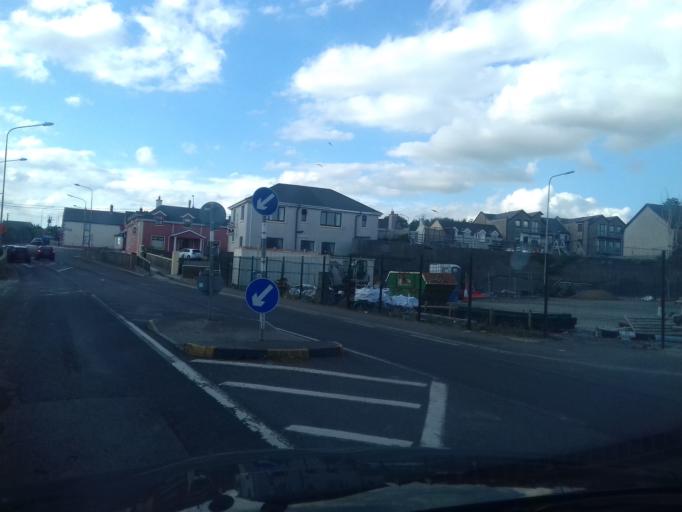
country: IE
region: Leinster
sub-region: Loch Garman
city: New Ross
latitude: 52.3976
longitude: -6.9352
